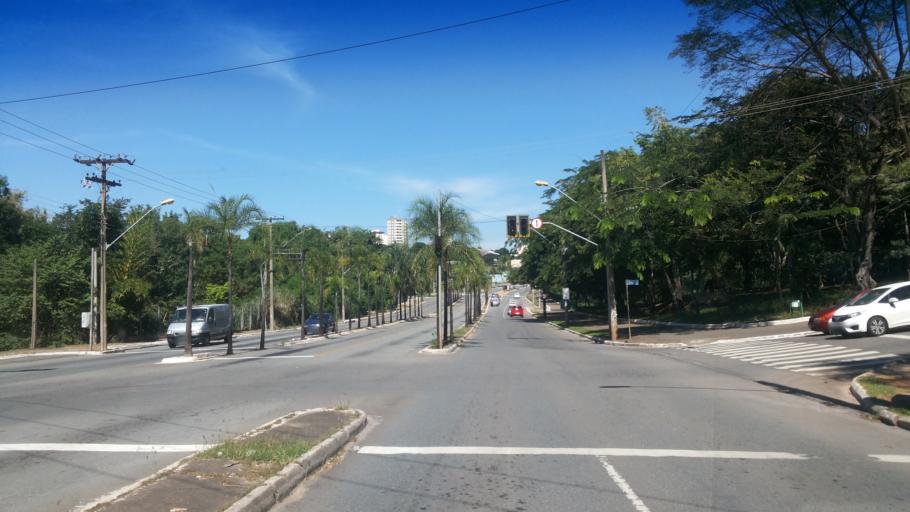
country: BR
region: Goias
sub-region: Goiania
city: Goiania
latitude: -16.7025
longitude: -49.2529
